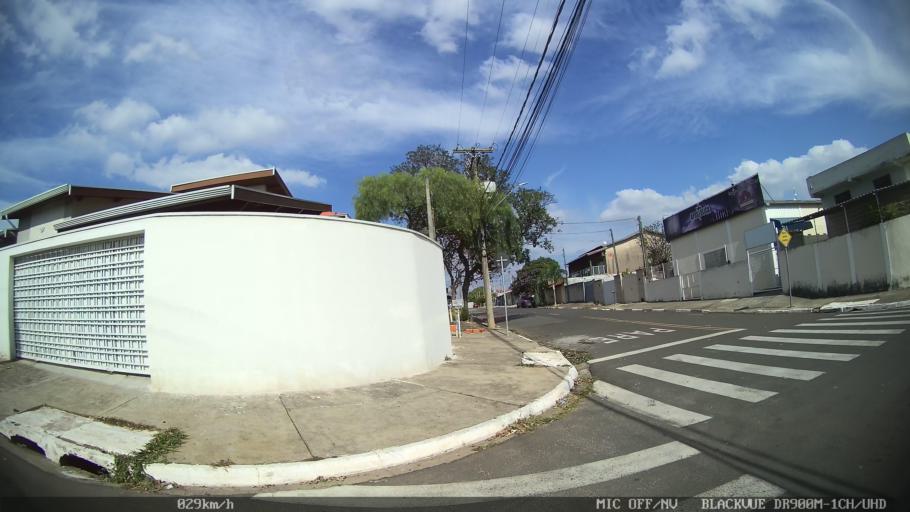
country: BR
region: Sao Paulo
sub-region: Hortolandia
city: Hortolandia
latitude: -22.9069
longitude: -47.2441
